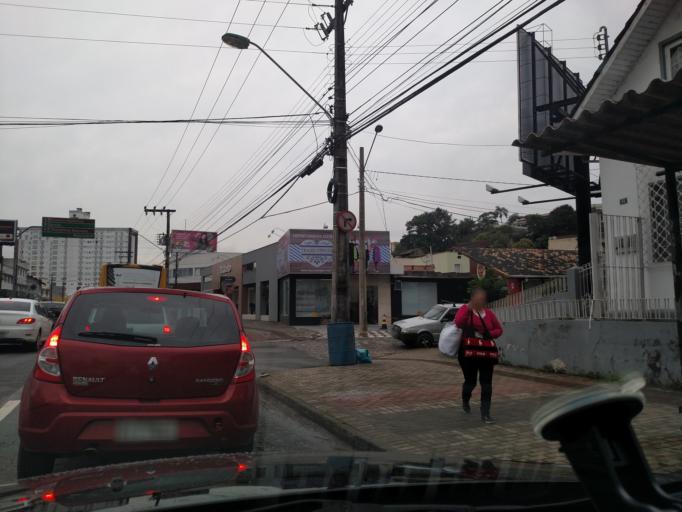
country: BR
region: Santa Catarina
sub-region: Blumenau
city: Blumenau
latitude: -26.9138
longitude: -49.0767
